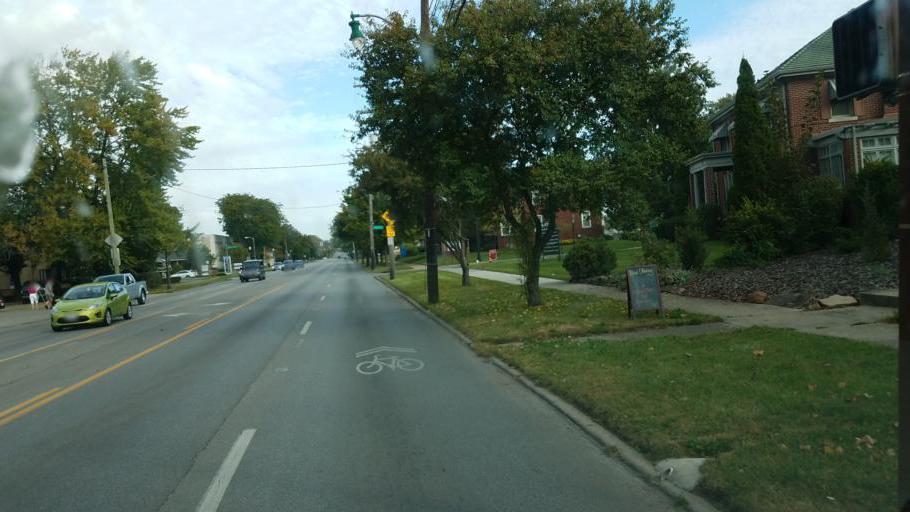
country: US
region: Ohio
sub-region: Franklin County
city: Worthington
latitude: 40.0379
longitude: -83.0175
